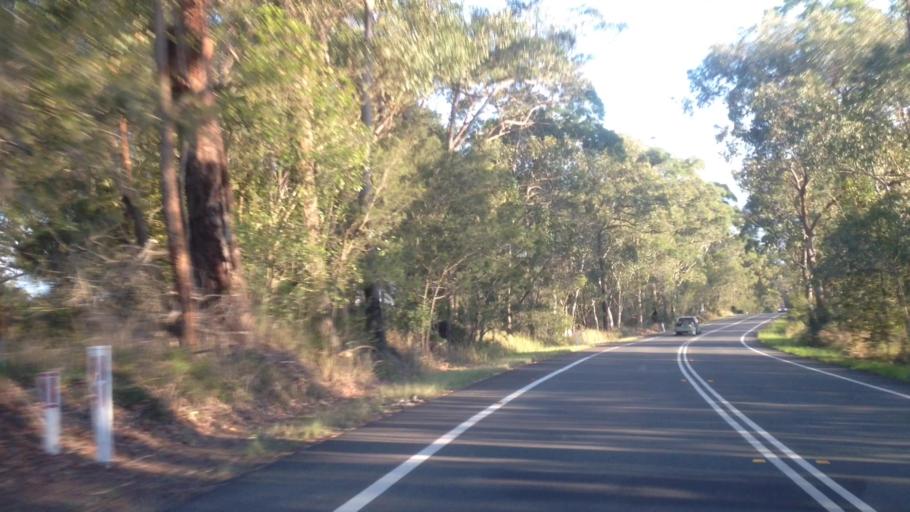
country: AU
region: New South Wales
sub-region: Lake Macquarie Shire
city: Dora Creek
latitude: -33.0224
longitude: 151.4944
